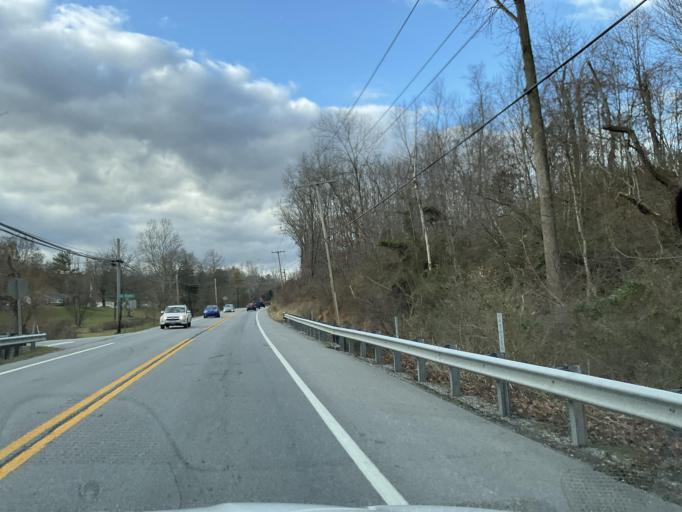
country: US
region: Pennsylvania
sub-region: Adams County
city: Mount Pleasant
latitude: 39.6741
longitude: -77.0335
